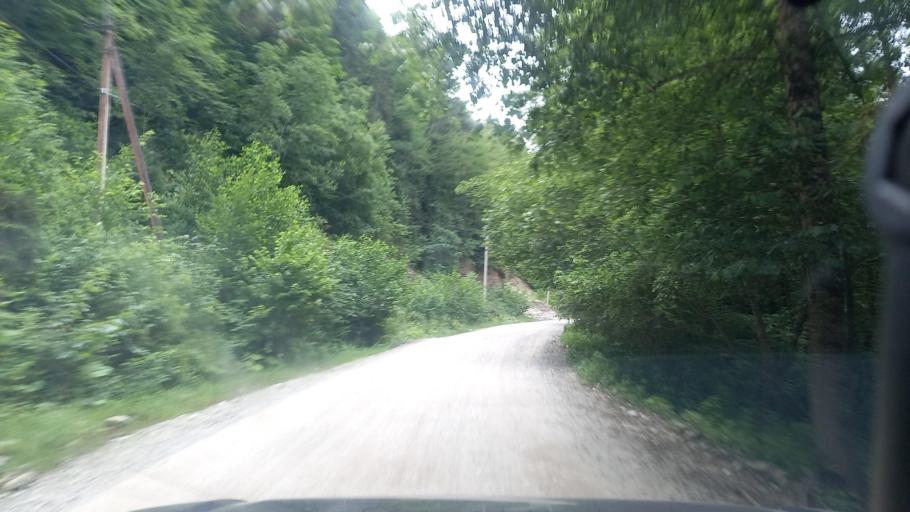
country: RU
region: Karachayevo-Cherkesiya
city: Kurdzhinovo
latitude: 43.8287
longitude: 40.9215
